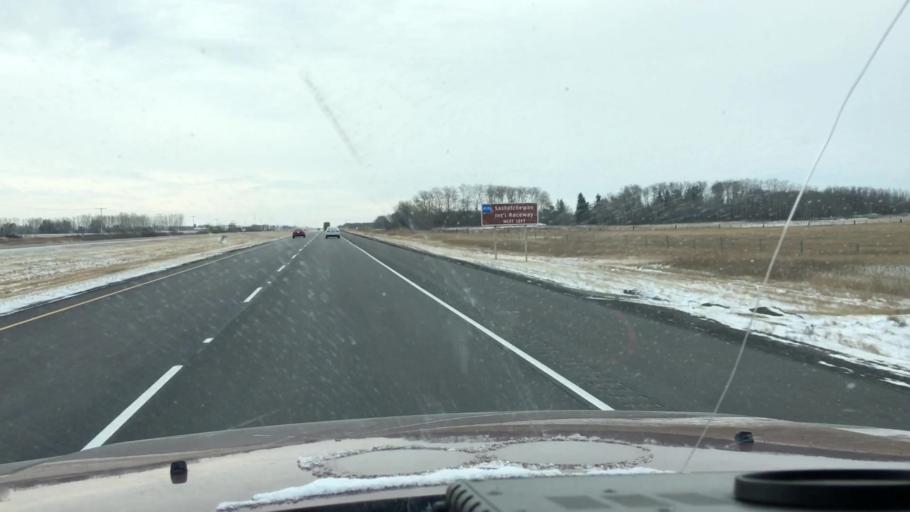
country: CA
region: Saskatchewan
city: Saskatoon
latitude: 51.9781
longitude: -106.5578
